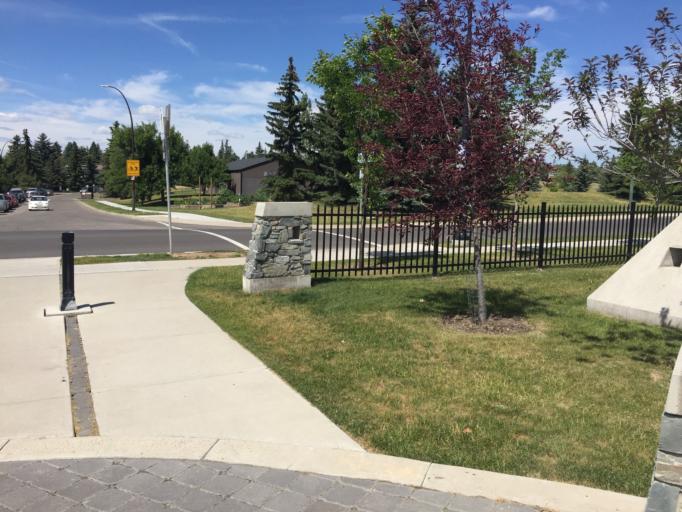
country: CA
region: Alberta
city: Calgary
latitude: 51.0178
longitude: -114.1344
